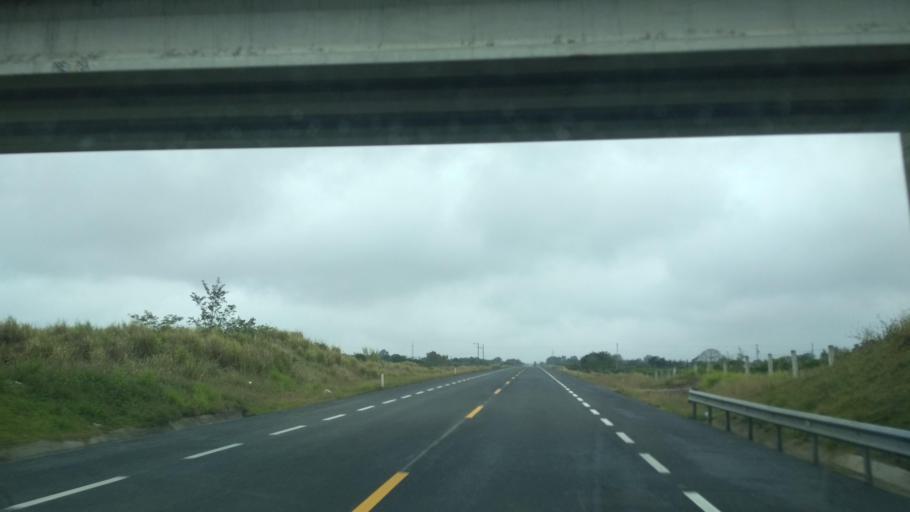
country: MX
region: Veracruz
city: Vega de San Marcos
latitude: 20.1681
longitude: -96.9584
